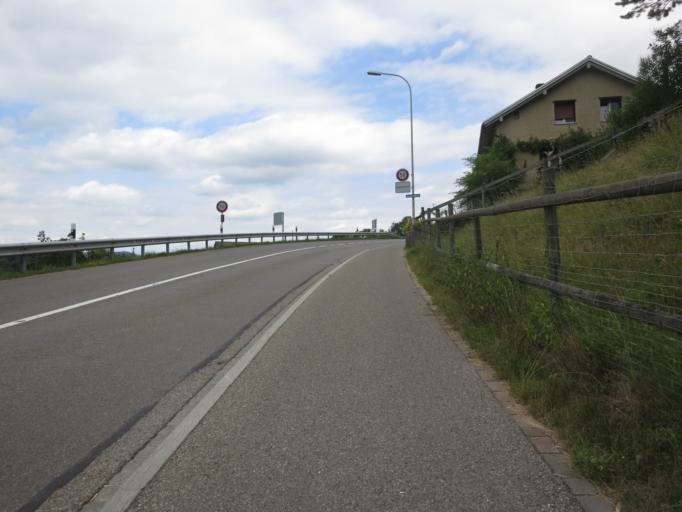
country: CH
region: Saint Gallen
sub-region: Wahlkreis Toggenburg
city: Ganterschwil
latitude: 47.3777
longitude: 9.0843
